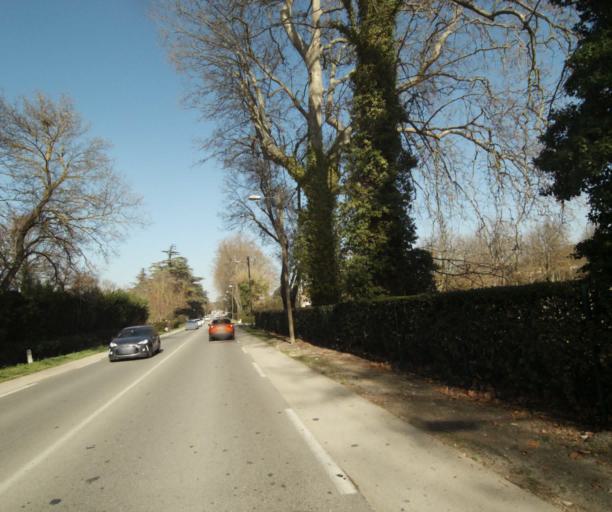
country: FR
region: Provence-Alpes-Cote d'Azur
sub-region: Departement des Bouches-du-Rhone
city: Bouc-Bel-Air
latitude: 43.4545
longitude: 5.4018
